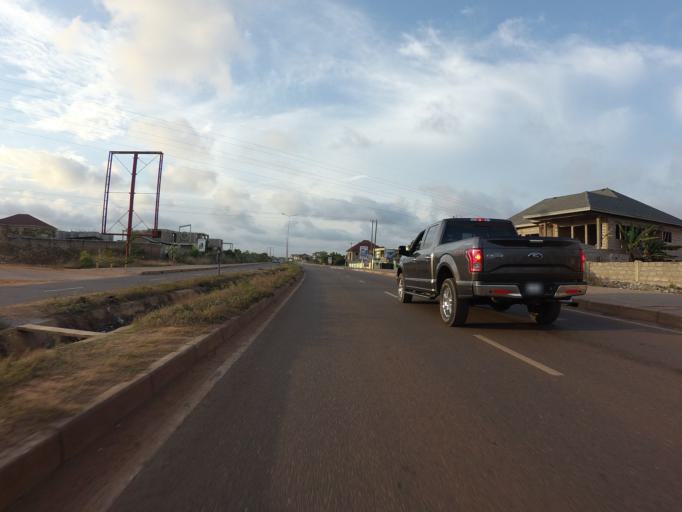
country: GH
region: Greater Accra
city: Teshi Old Town
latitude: 5.6016
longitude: -0.1372
